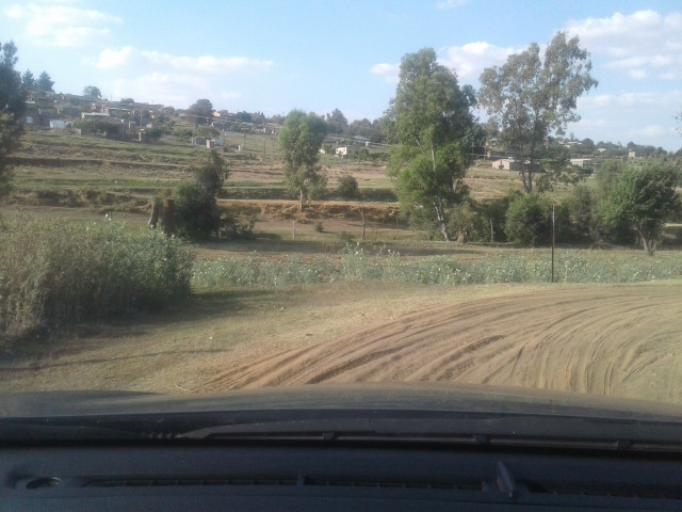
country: LS
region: Berea
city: Teyateyaneng
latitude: -29.1542
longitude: 27.7559
